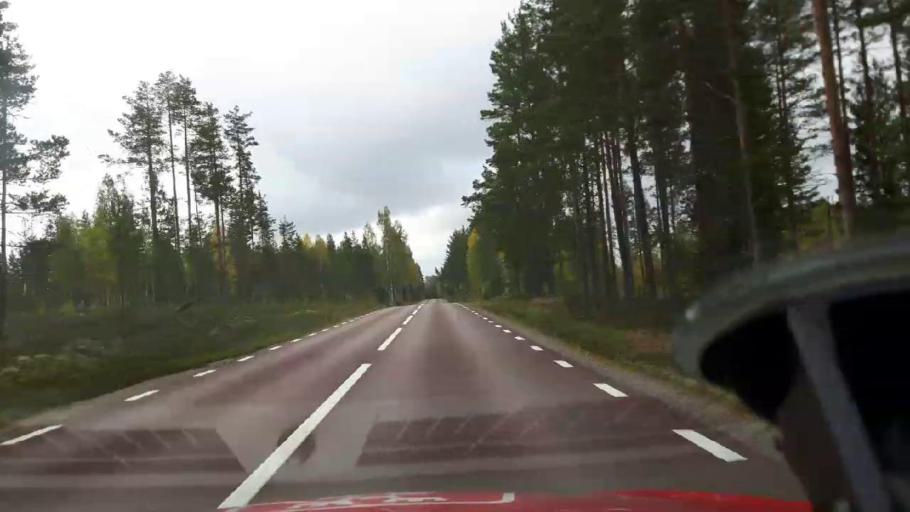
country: SE
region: Jaemtland
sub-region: Harjedalens Kommun
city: Sveg
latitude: 62.2046
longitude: 14.8492
